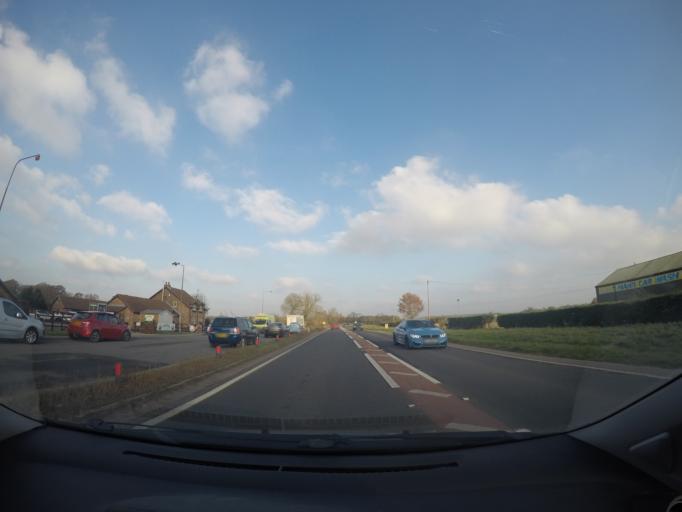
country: GB
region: England
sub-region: City of York
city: Murton
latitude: 54.0021
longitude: -1.0126
